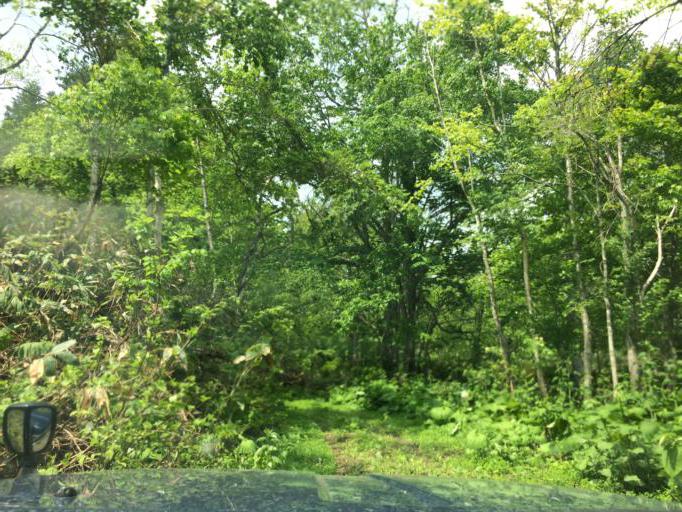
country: JP
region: Hokkaido
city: Niseko Town
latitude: 42.7156
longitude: 140.5427
